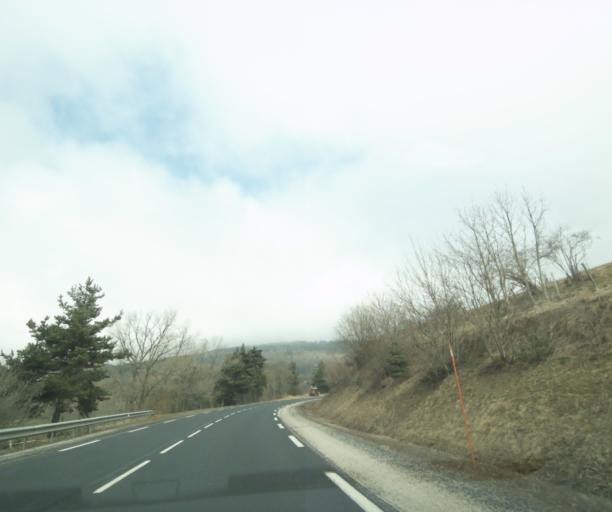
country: FR
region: Languedoc-Roussillon
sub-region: Departement de la Lozere
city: Langogne
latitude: 44.7557
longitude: 3.8846
